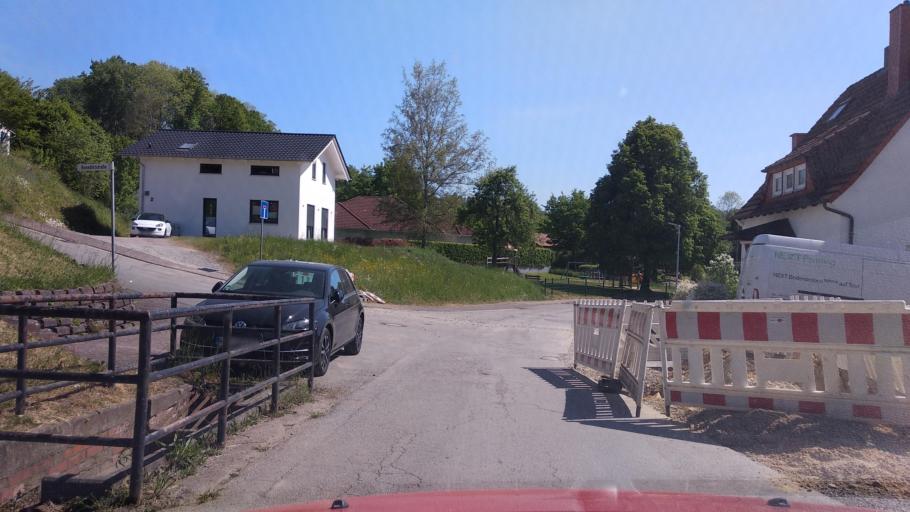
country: DE
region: Lower Saxony
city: Bad Karlshafen
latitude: 51.6369
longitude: 9.4163
